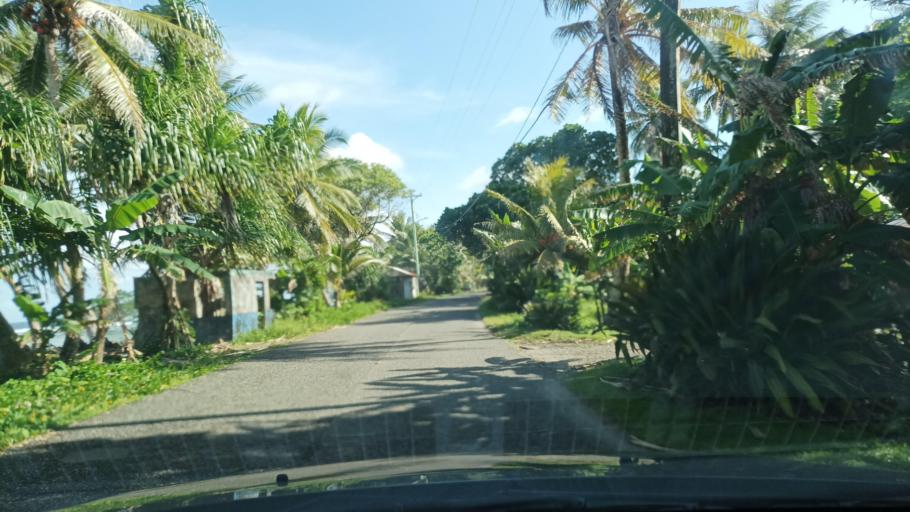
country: FM
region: Kosrae
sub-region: Malem Municipality
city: Malem
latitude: 5.2848
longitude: 163.0256
